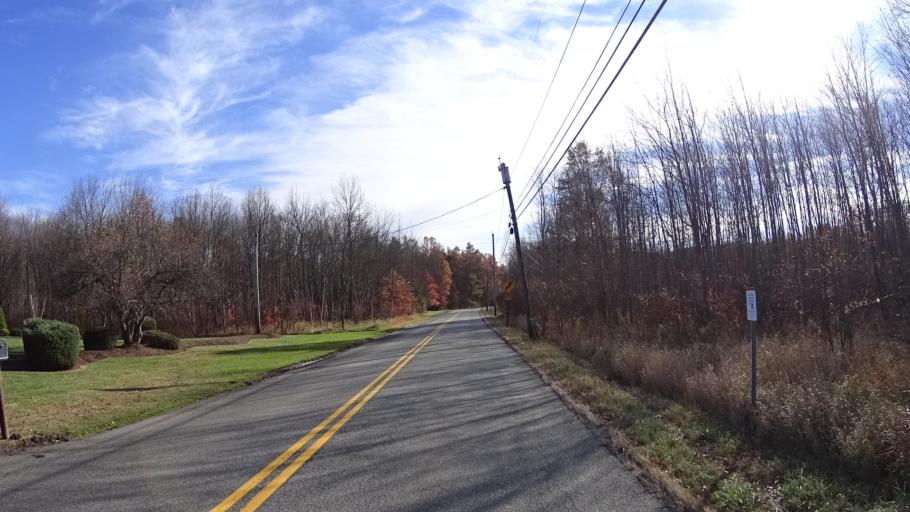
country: US
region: New Jersey
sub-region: Union County
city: Berkeley Heights
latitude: 40.7041
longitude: -74.4759
